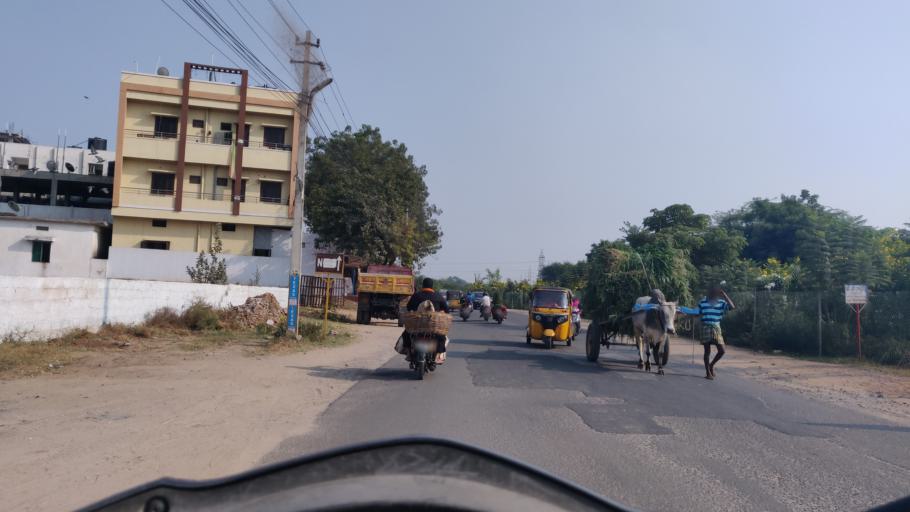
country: IN
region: Telangana
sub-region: Rangareddi
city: Uppal Kalan
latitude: 17.4006
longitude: 78.5825
